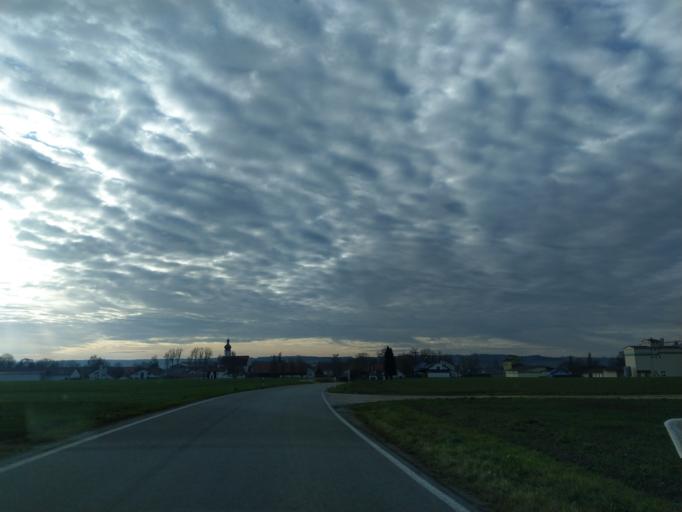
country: DE
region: Bavaria
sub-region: Lower Bavaria
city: Buchhofen
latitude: 48.7017
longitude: 12.9233
